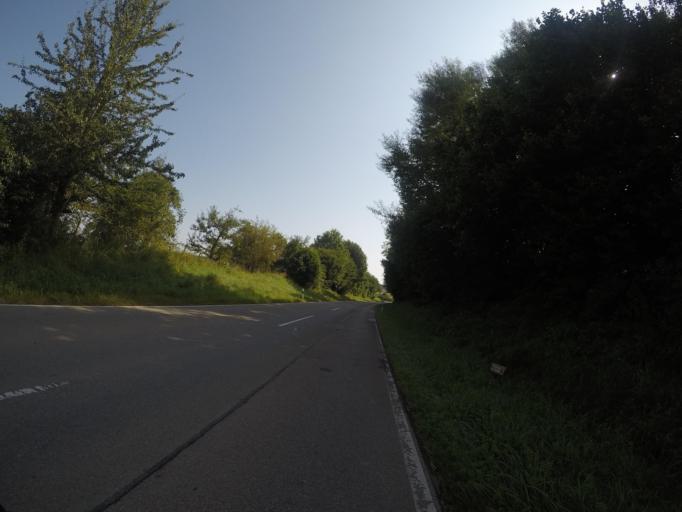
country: DE
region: Baden-Wuerttemberg
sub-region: Tuebingen Region
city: Wain
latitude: 48.1893
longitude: 10.0296
